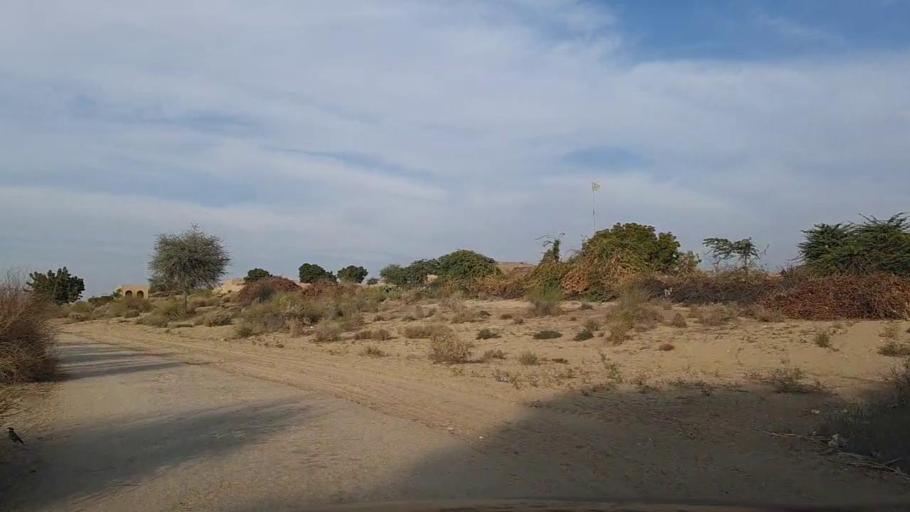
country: PK
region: Sindh
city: Jam Sahib
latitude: 26.4555
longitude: 68.5698
